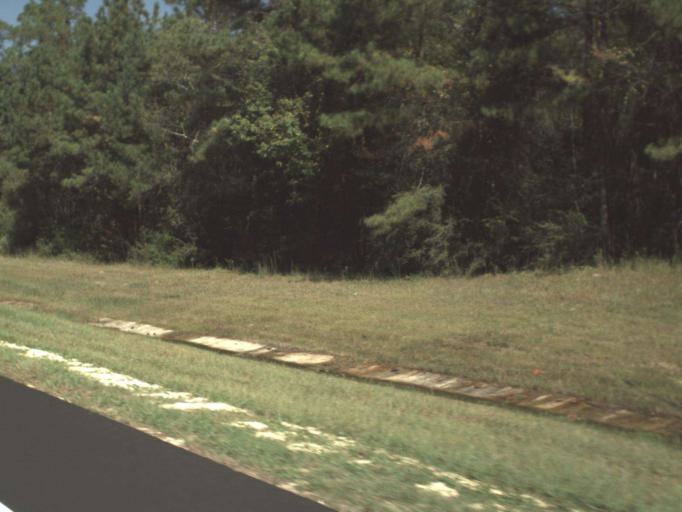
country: US
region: Alabama
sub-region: Covington County
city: Florala
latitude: 30.8580
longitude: -86.2487
